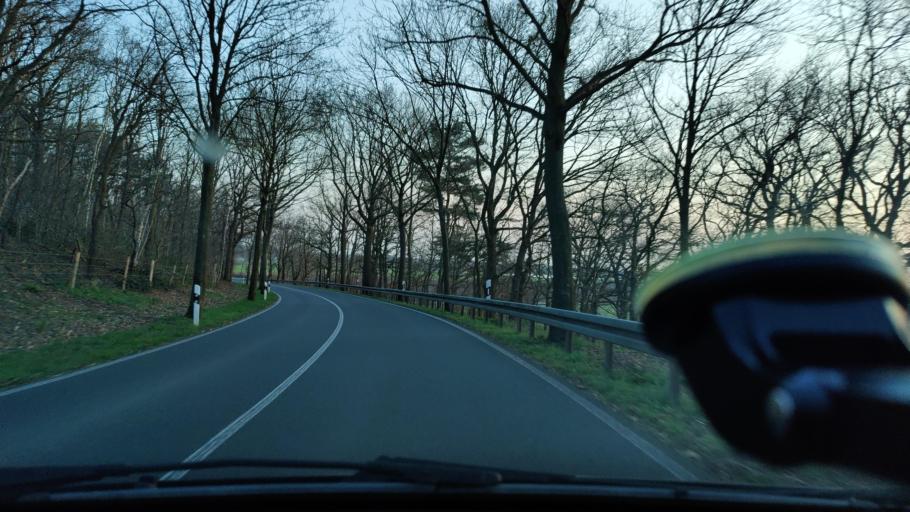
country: NL
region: Limburg
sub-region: Gemeente Bergen
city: Wellerlooi
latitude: 51.6088
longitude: 6.1116
